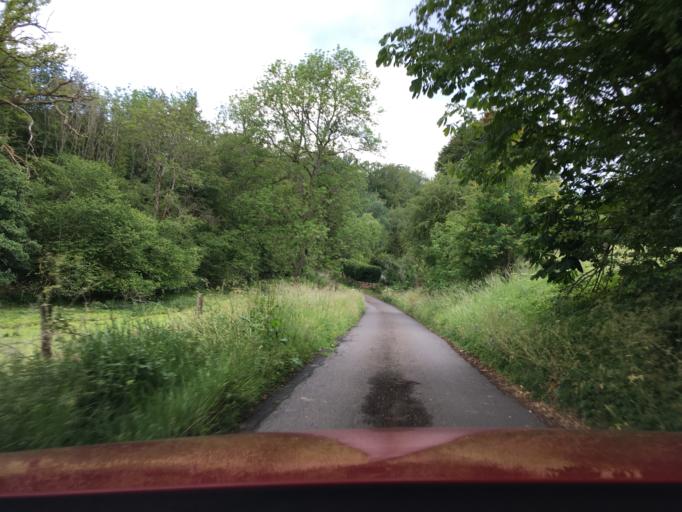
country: GB
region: England
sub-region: Gloucestershire
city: Shurdington
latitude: 51.7914
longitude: -2.0782
